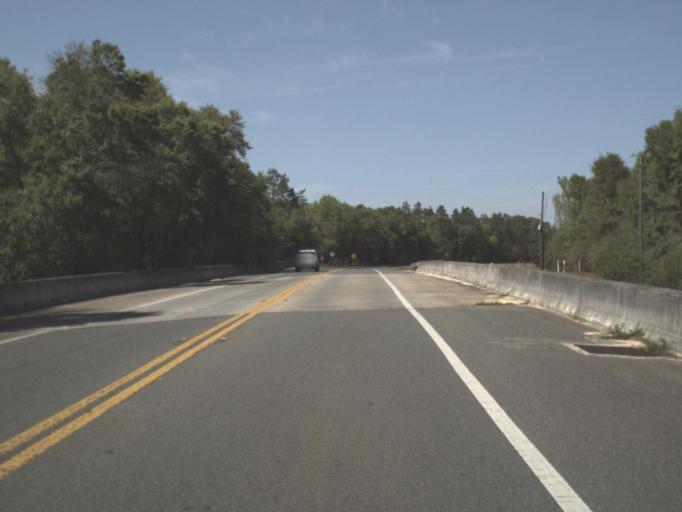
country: US
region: Florida
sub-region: Okaloosa County
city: Crestview
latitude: 30.7344
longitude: -86.6539
